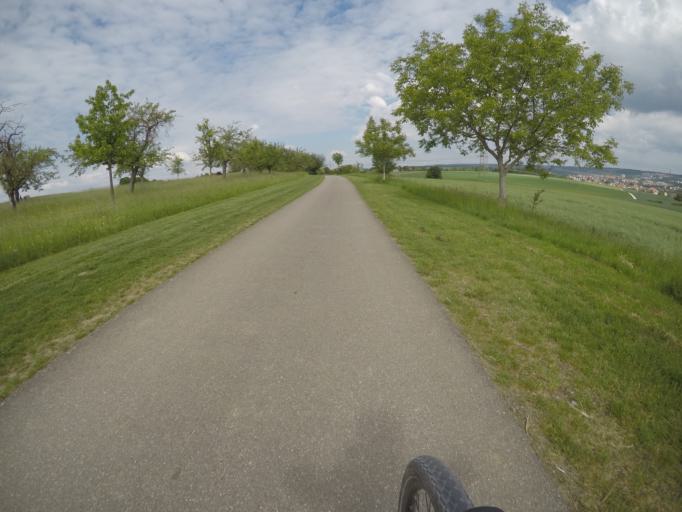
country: DE
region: Baden-Wuerttemberg
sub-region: Regierungsbezirk Stuttgart
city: Wernau
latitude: 48.6716
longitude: 9.4238
